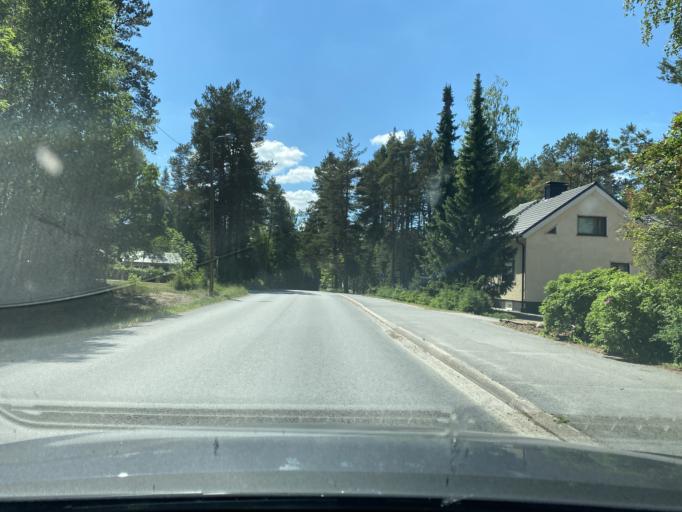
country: FI
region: Satakunta
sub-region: Rauma
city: Eura
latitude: 61.1306
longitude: 22.1665
